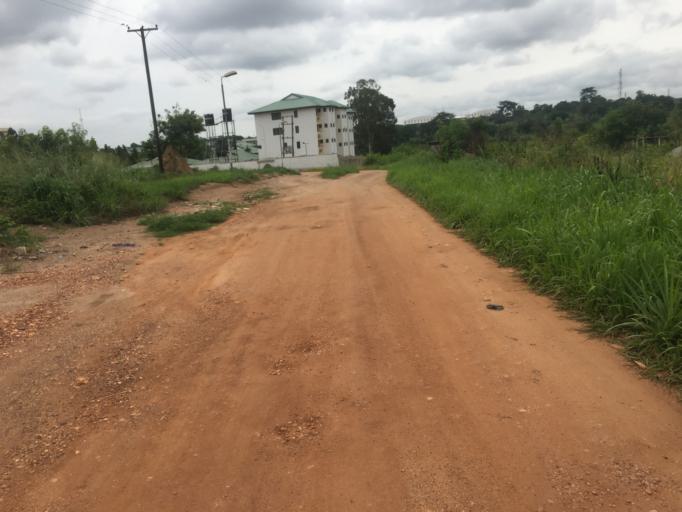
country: GH
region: Ashanti
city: Mamponteng
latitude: 6.6890
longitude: -1.5540
